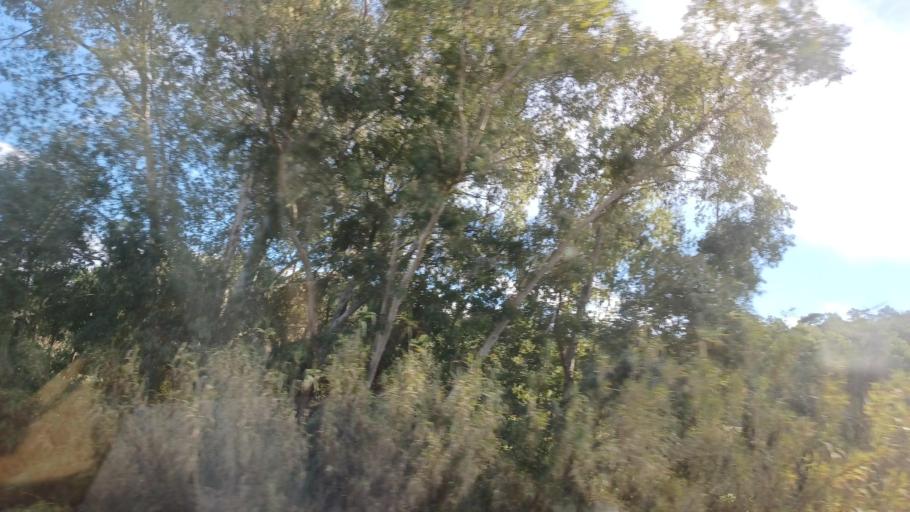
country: CY
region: Lefkosia
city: Lythrodontas
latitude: 34.9320
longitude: 33.2984
